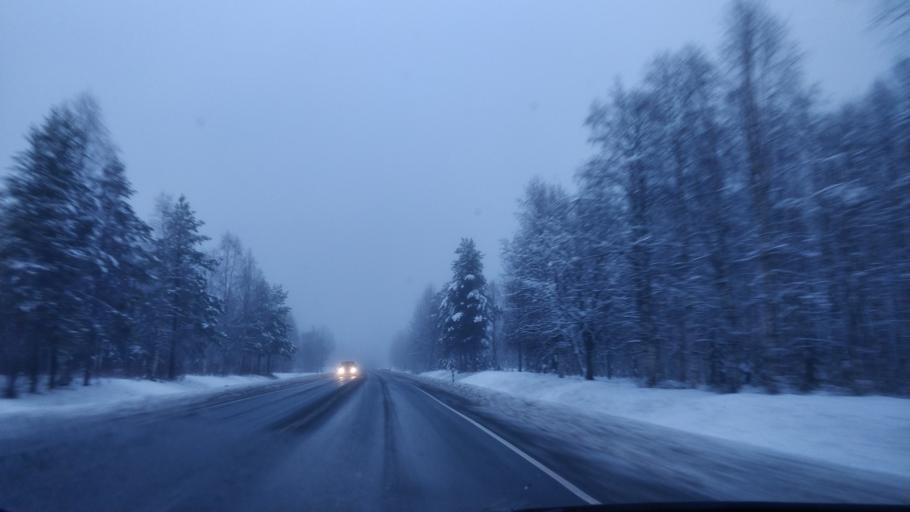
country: FI
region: Lapland
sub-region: Kemi-Tornio
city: Tervola
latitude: 66.1538
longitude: 25.0384
